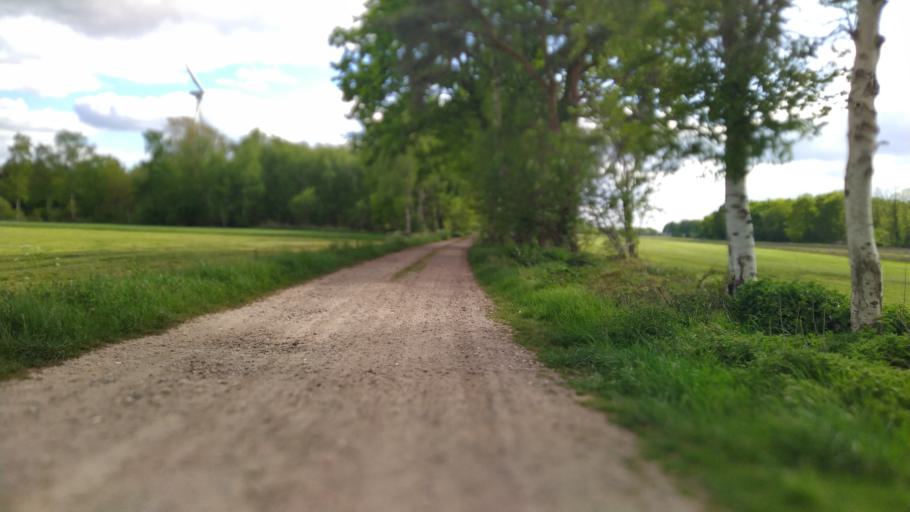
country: DE
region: Lower Saxony
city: Brest
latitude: 53.4396
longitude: 9.3865
